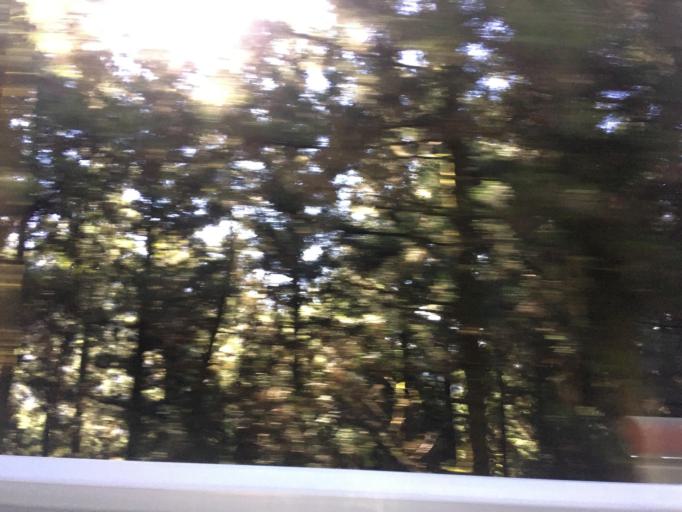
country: TW
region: Taiwan
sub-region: Yilan
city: Yilan
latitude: 24.5007
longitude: 121.5536
